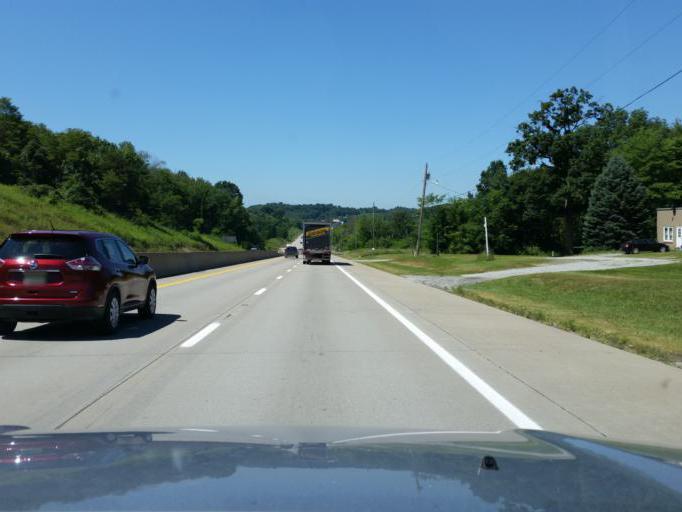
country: US
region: Pennsylvania
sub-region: Westmoreland County
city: Delmont
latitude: 40.4021
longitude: -79.5498
